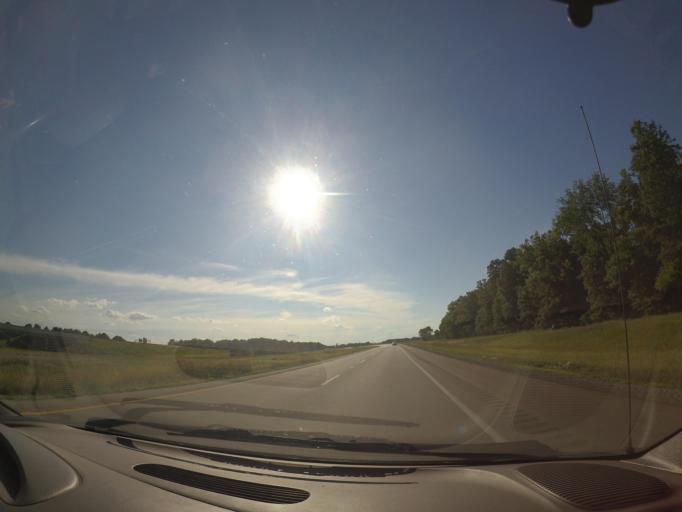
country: US
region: Ohio
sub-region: Henry County
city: Liberty Center
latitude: 41.4162
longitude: -84.0624
